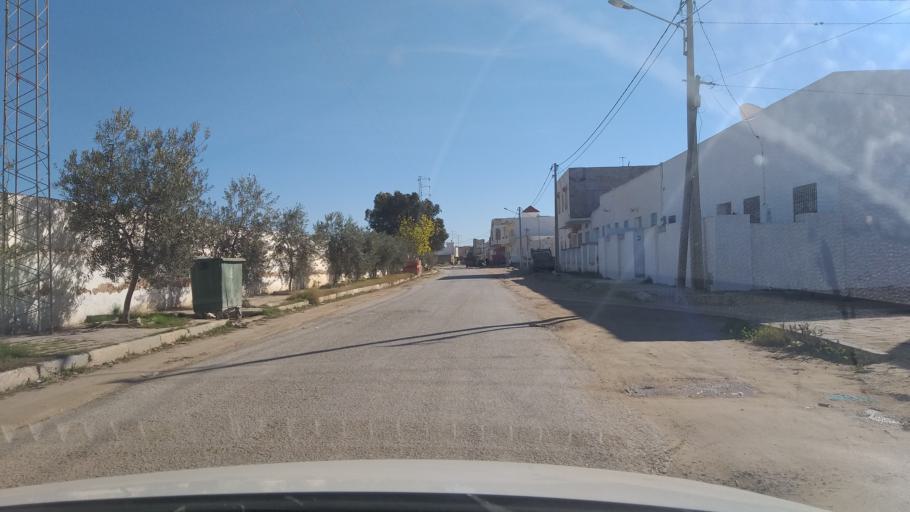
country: TN
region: Al Mahdiyah
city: El Jem
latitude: 35.2945
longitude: 10.7134
